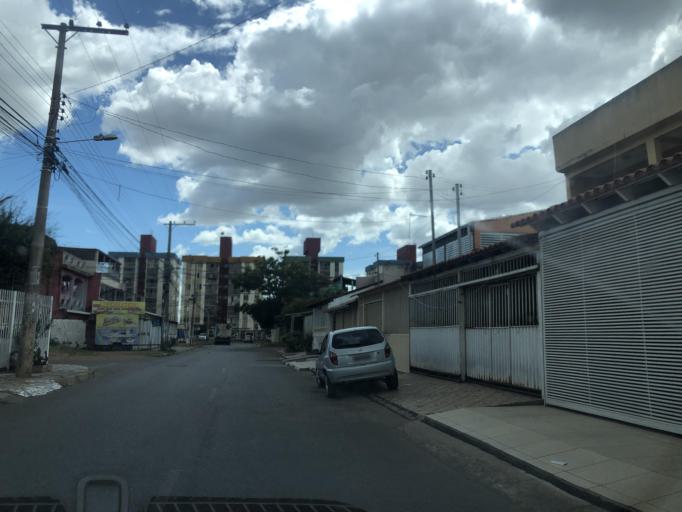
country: BR
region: Federal District
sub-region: Brasilia
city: Brasilia
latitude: -15.8685
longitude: -48.0631
